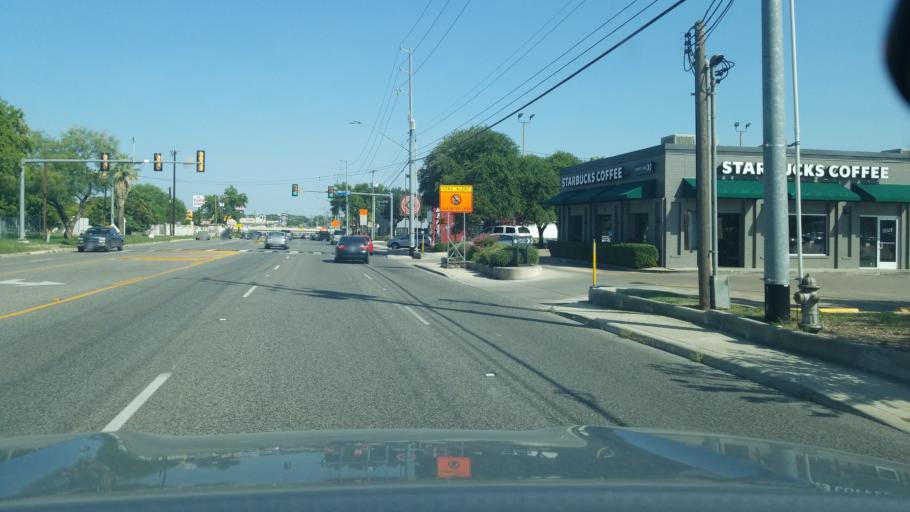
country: US
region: Texas
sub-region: Bexar County
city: Hollywood Park
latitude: 29.5671
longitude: -98.4855
